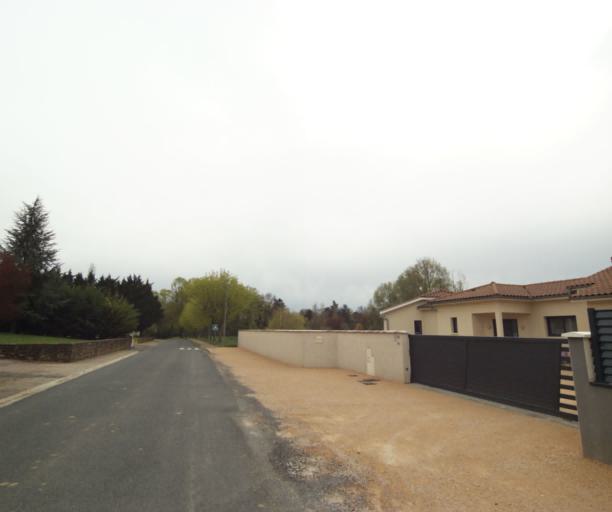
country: FR
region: Bourgogne
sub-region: Departement de Saone-et-Loire
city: Charnay-les-Macon
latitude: 46.3158
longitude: 4.7935
